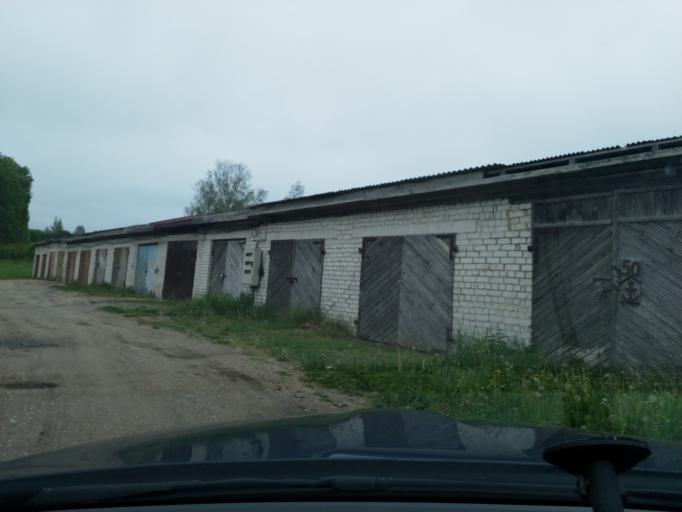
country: LV
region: Kuldigas Rajons
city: Kuldiga
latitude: 56.8796
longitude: 21.8222
